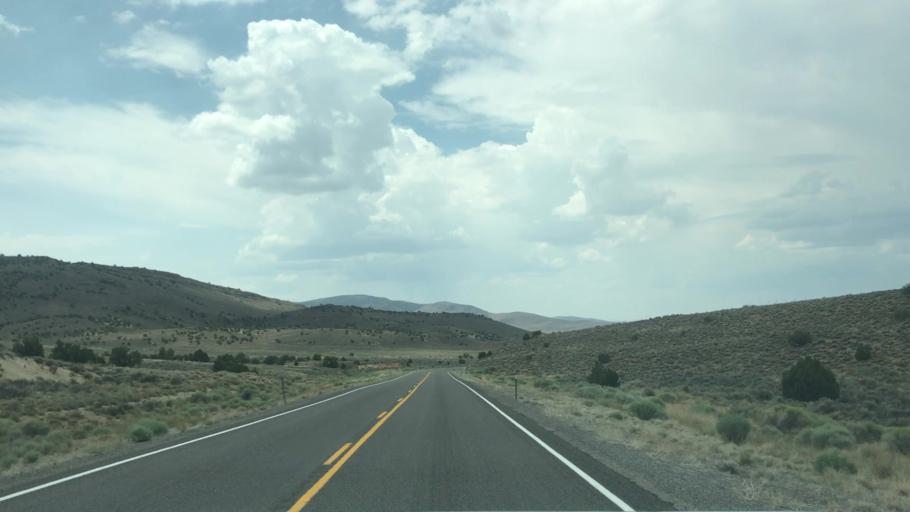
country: US
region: Nevada
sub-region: Eureka County
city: Eureka
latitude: 39.4030
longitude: -115.7024
